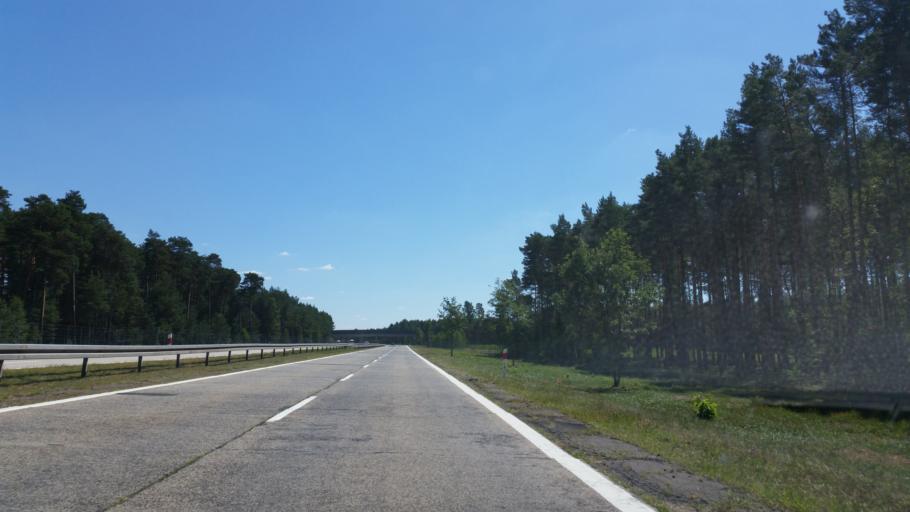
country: PL
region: Lubusz
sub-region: Powiat zaganski
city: Malomice
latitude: 51.4373
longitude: 15.3625
